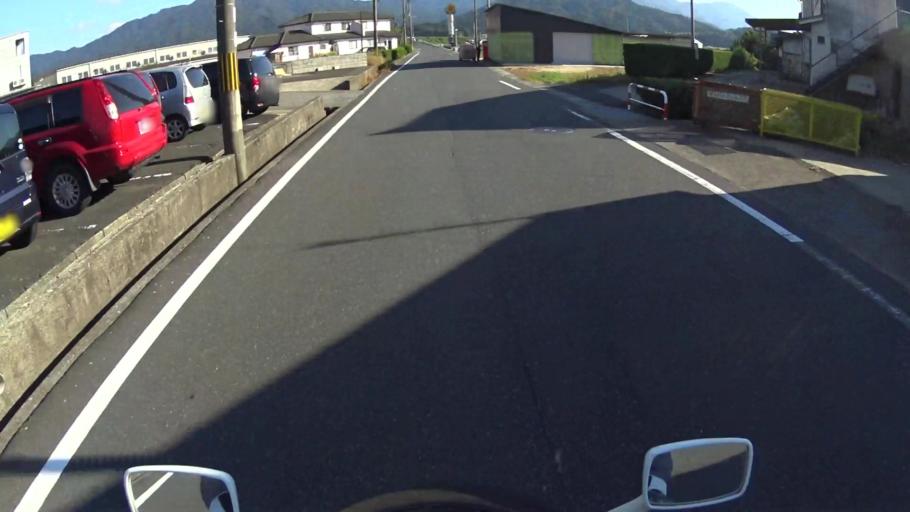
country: JP
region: Kyoto
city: Miyazu
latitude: 35.5355
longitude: 135.1143
